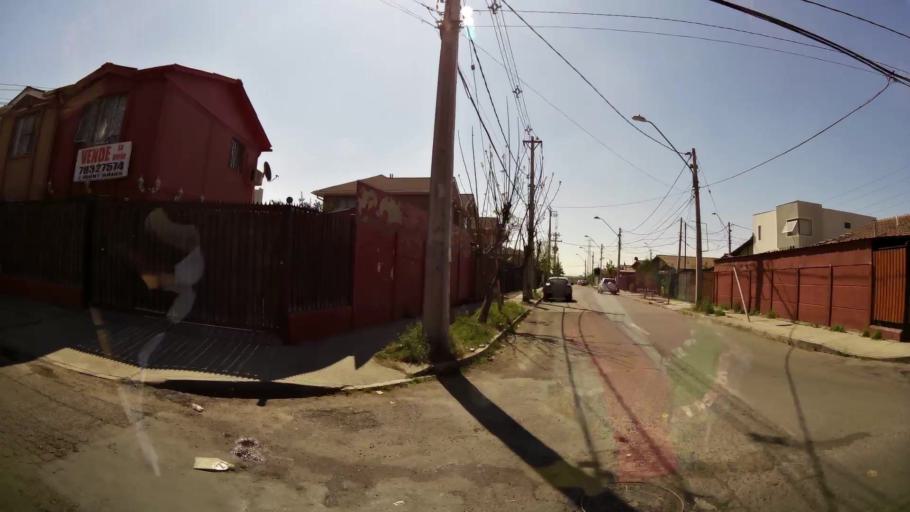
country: CL
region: Santiago Metropolitan
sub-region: Provincia de Santiago
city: Lo Prado
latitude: -33.3495
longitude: -70.7440
